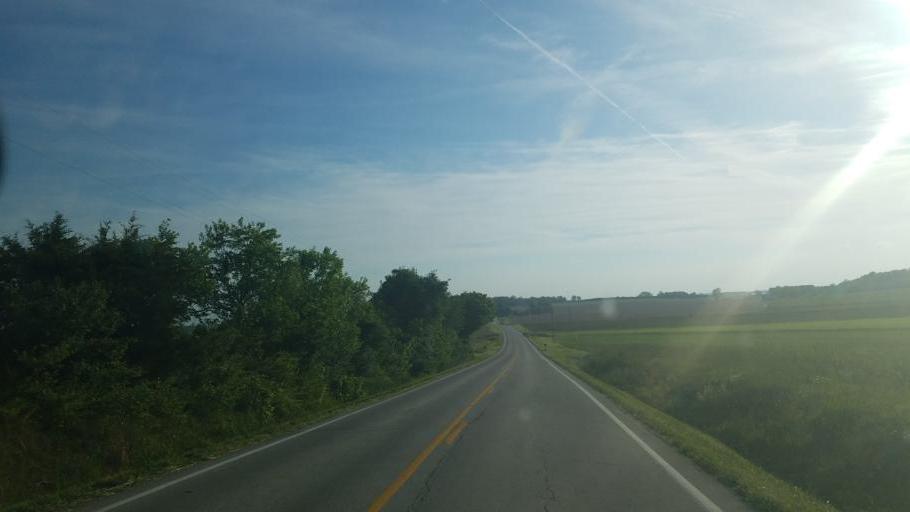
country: US
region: Ohio
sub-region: Highland County
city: Greenfield
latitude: 39.4050
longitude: -83.3024
